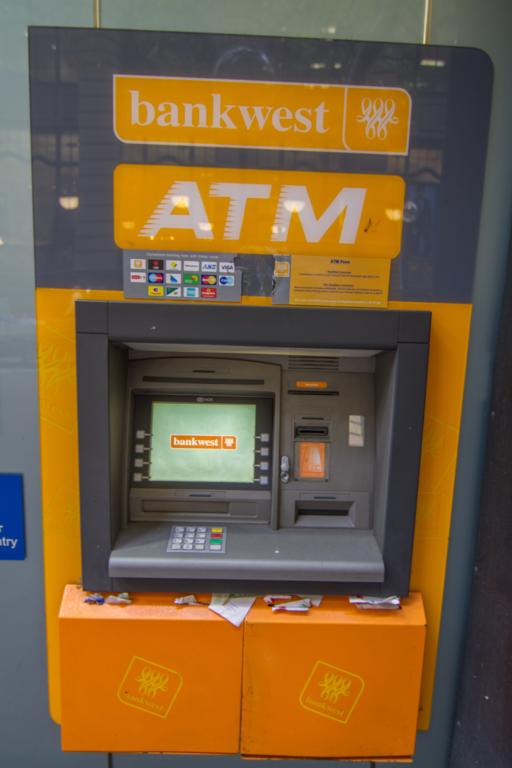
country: AU
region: New South Wales
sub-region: City of Sydney
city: Sydney
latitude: -33.8679
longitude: 151.2070
